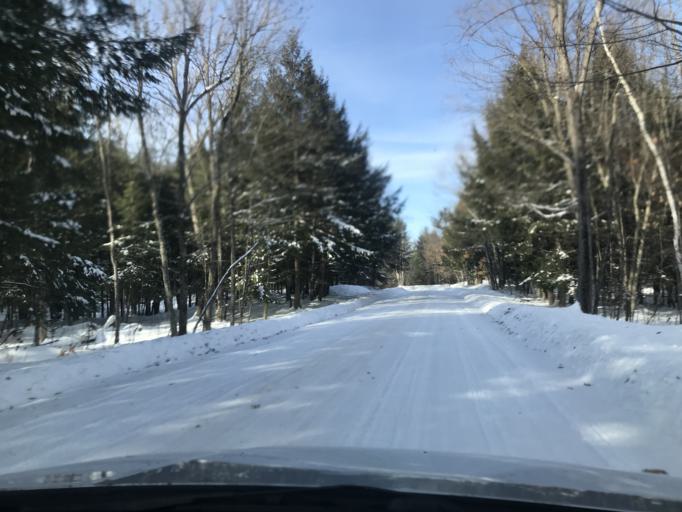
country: US
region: Wisconsin
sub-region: Oconto County
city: Gillett
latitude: 45.1490
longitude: -88.2374
